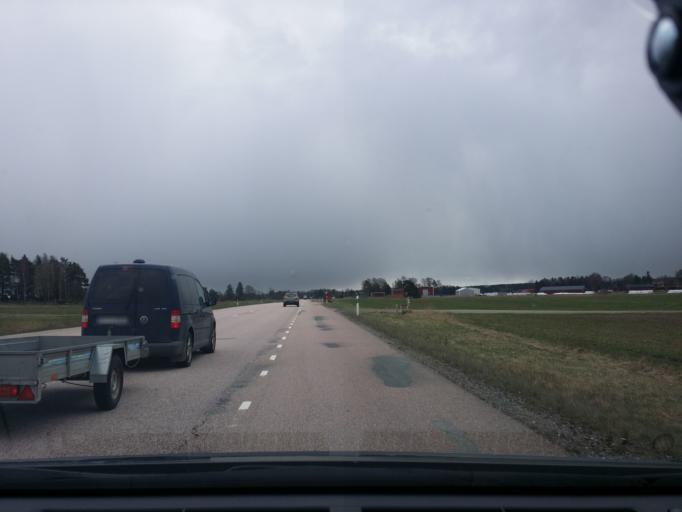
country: SE
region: Uppsala
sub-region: Enkopings Kommun
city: Enkoping
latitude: 59.6904
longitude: 17.0314
